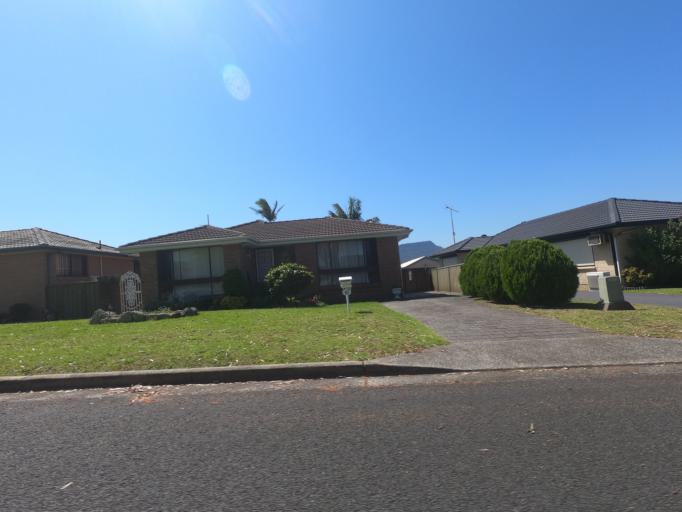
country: AU
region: New South Wales
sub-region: Wollongong
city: Dapto
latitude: -34.4907
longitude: 150.7824
